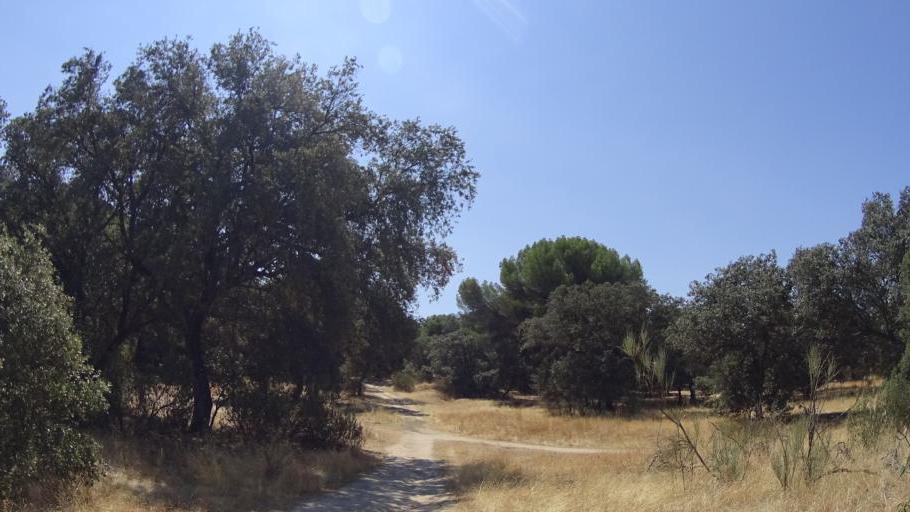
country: ES
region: Madrid
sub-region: Provincia de Madrid
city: Boadilla del Monte
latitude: 40.4365
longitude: -3.8730
